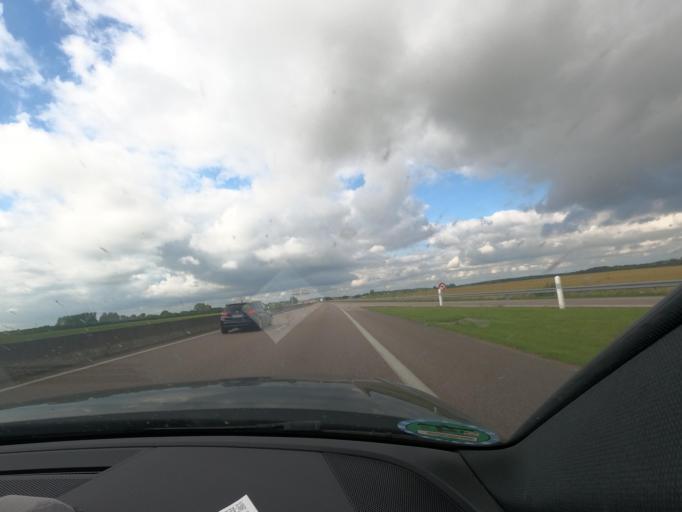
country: FR
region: Haute-Normandie
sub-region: Departement de la Seine-Maritime
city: Aumale
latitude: 49.7630
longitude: 1.7067
